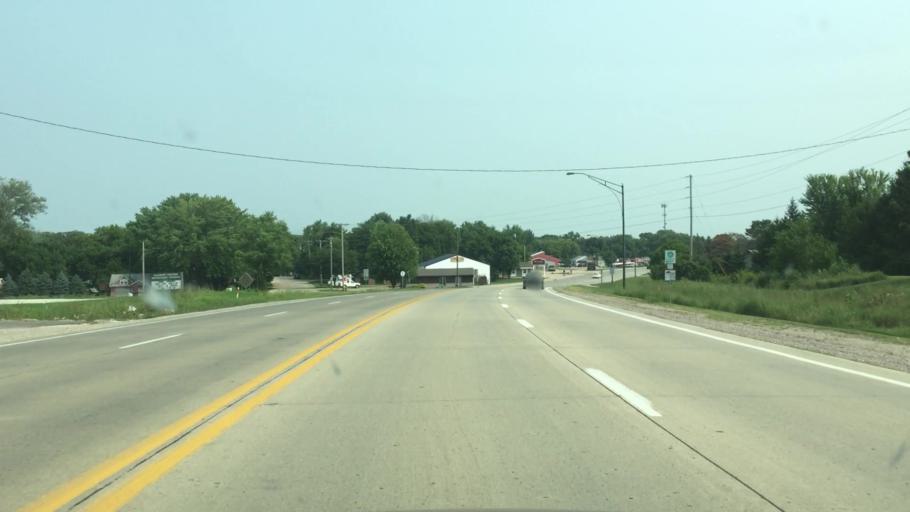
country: US
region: Iowa
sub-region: Dickinson County
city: Arnolds Park
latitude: 43.3592
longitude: -95.1417
